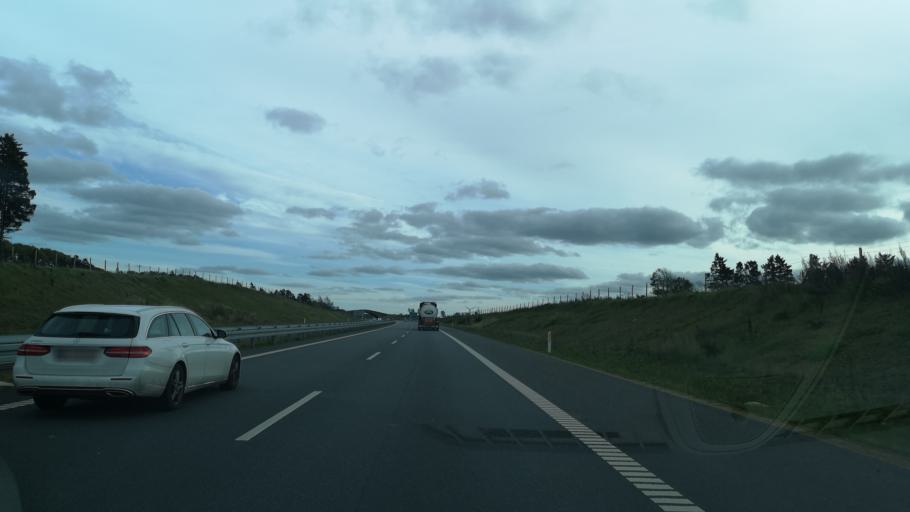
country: DK
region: Central Jutland
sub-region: Herning Kommune
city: Avlum
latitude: 56.2860
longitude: 8.7333
